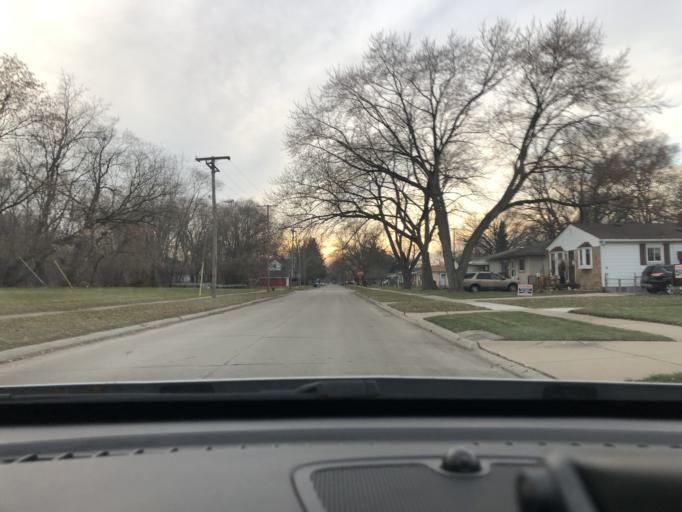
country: US
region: Michigan
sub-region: Wayne County
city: Allen Park
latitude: 42.2737
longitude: -83.2277
